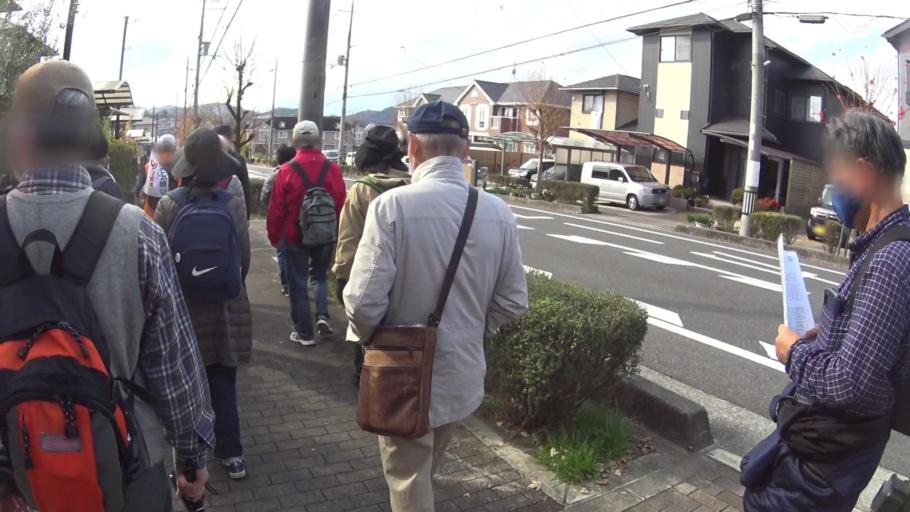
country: JP
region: Nara
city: Kashihara-shi
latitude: 34.4746
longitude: 135.8038
